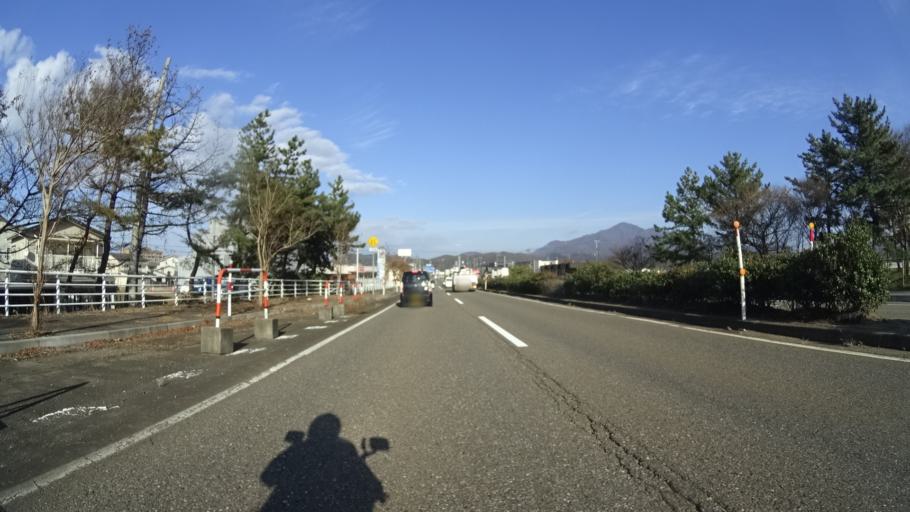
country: JP
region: Niigata
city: Kashiwazaki
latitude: 37.2717
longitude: 138.3894
